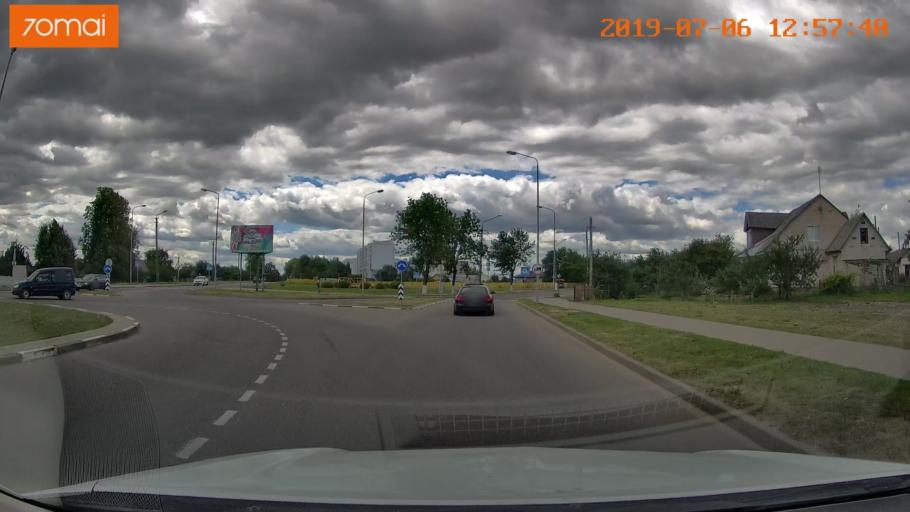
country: BY
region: Minsk
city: Dzyarzhynsk
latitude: 53.6870
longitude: 27.1511
